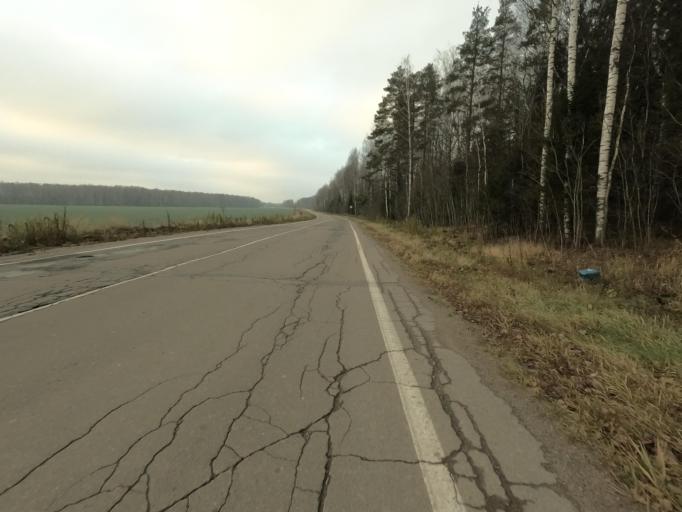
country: RU
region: Leningrad
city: Mga
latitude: 59.7962
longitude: 31.0038
